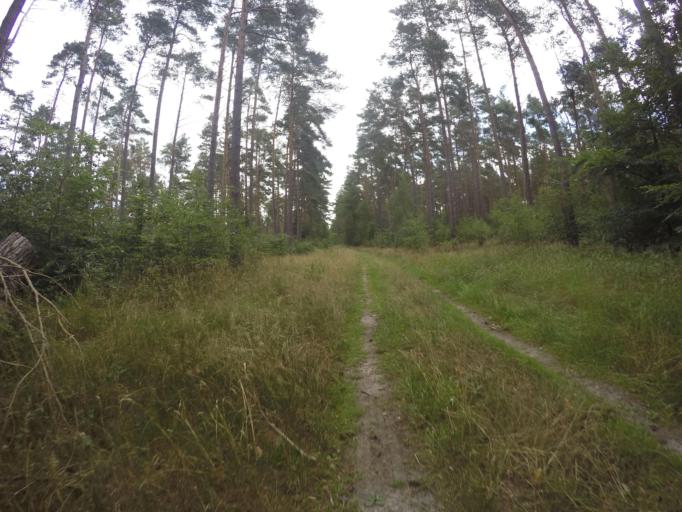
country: DE
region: Lower Saxony
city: Thomasburg
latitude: 53.2522
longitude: 10.6686
